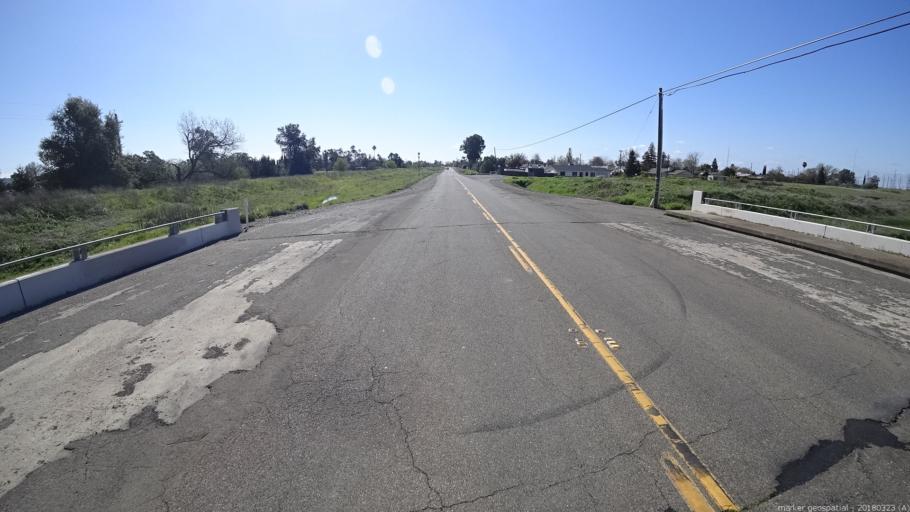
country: US
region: California
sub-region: Sacramento County
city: Elverta
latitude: 38.7262
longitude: -121.4700
